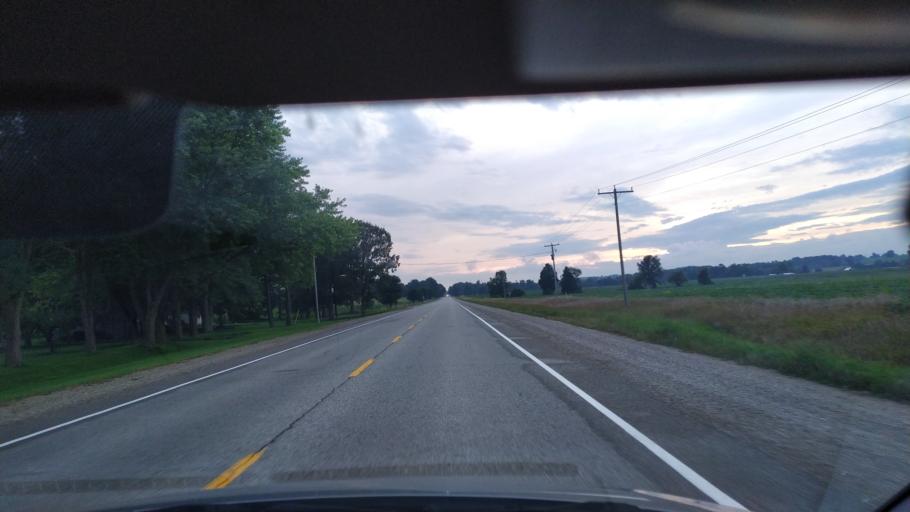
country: CA
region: Ontario
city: Kitchener
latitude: 43.3186
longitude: -80.5245
